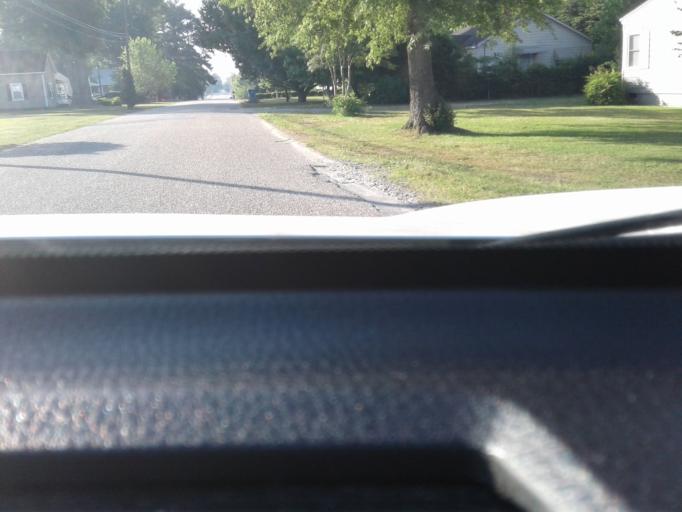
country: US
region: North Carolina
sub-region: Harnett County
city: Dunn
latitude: 35.3167
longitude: -78.6207
